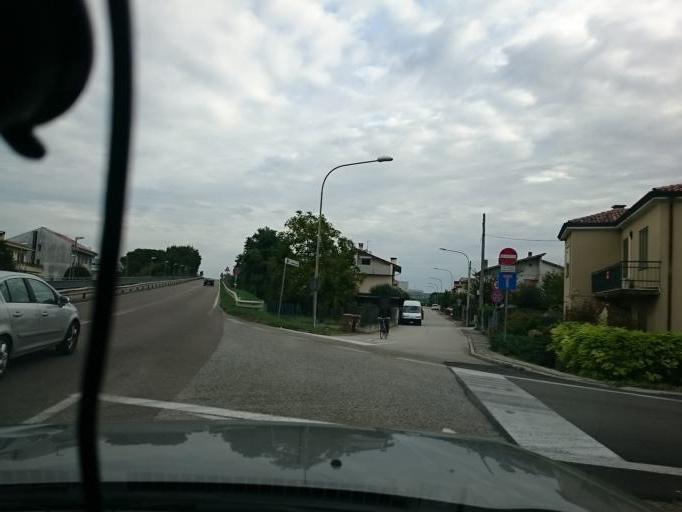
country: IT
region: Veneto
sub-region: Provincia di Vicenza
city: Grisignano di Zocco
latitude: 45.4769
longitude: 11.7030
